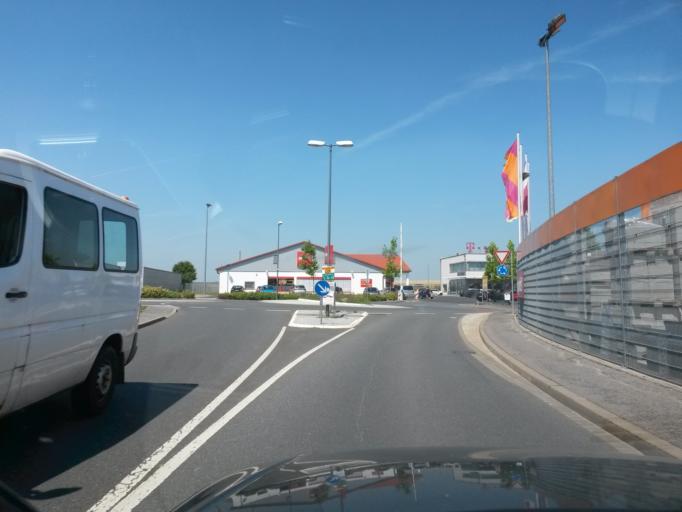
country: DE
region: Bavaria
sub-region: Regierungsbezirk Unterfranken
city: Estenfeld
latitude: 49.8157
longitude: 9.9820
